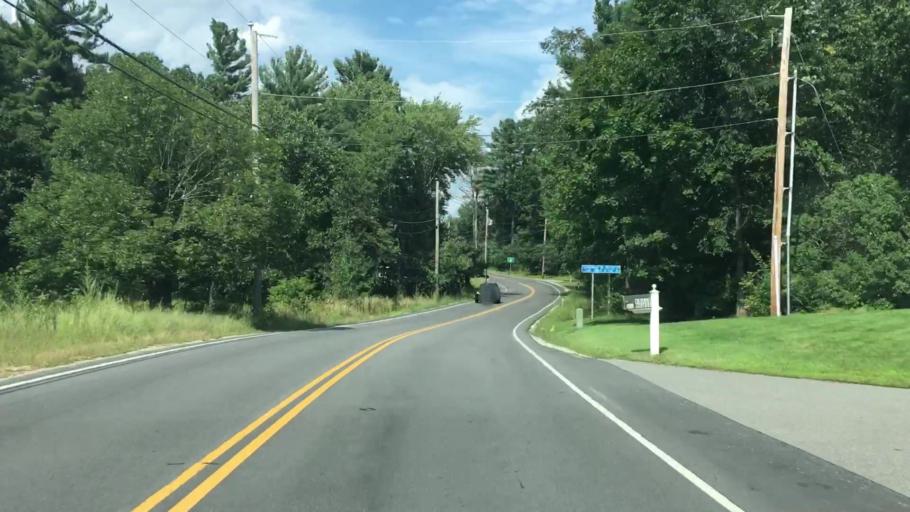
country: US
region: New Hampshire
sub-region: Rockingham County
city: Windham
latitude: 42.7996
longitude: -71.3522
